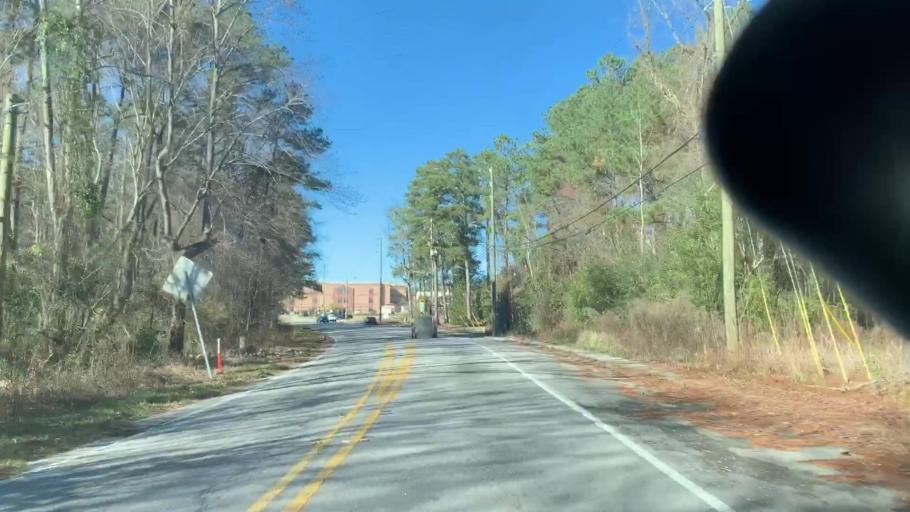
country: US
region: South Carolina
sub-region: Richland County
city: Woodfield
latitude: 34.0808
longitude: -80.9229
